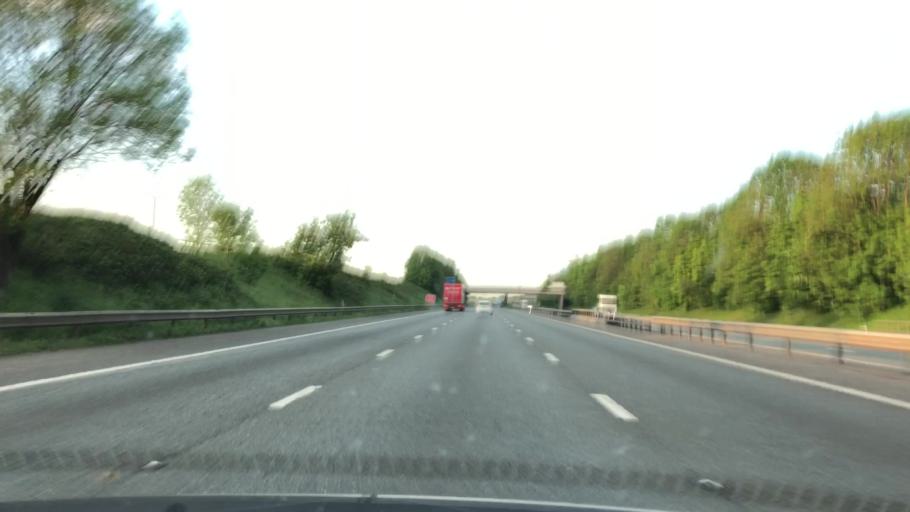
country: GB
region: England
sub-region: Cheshire West and Chester
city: Elton
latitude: 53.2569
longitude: -2.8291
